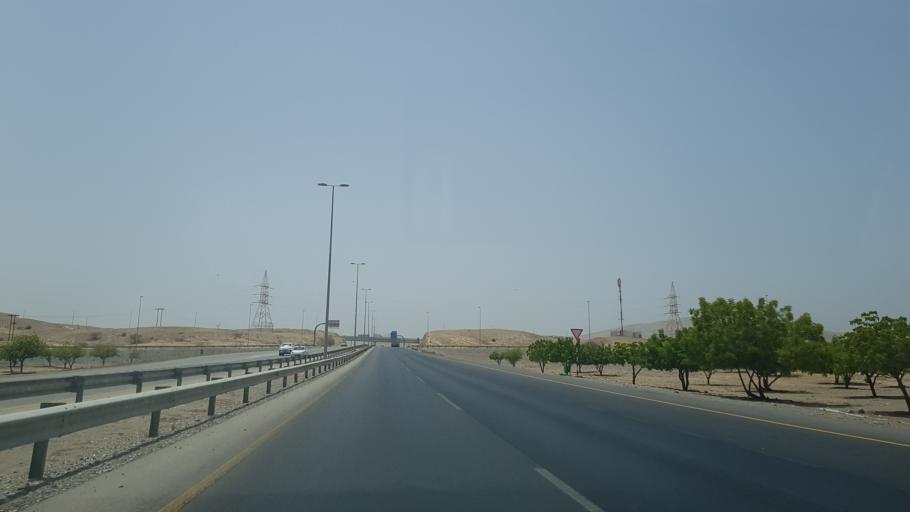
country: OM
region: Muhafazat Masqat
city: As Sib al Jadidah
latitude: 23.5731
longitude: 58.1922
